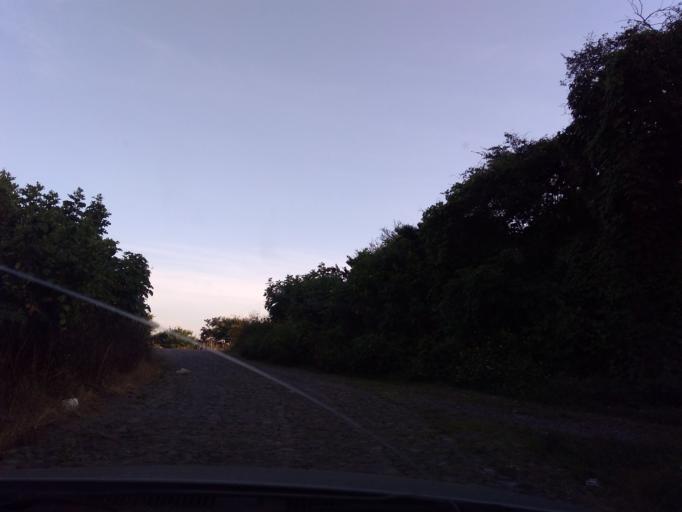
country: MX
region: Jalisco
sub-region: Tonila
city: San Marcos
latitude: 19.4574
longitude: -103.5197
